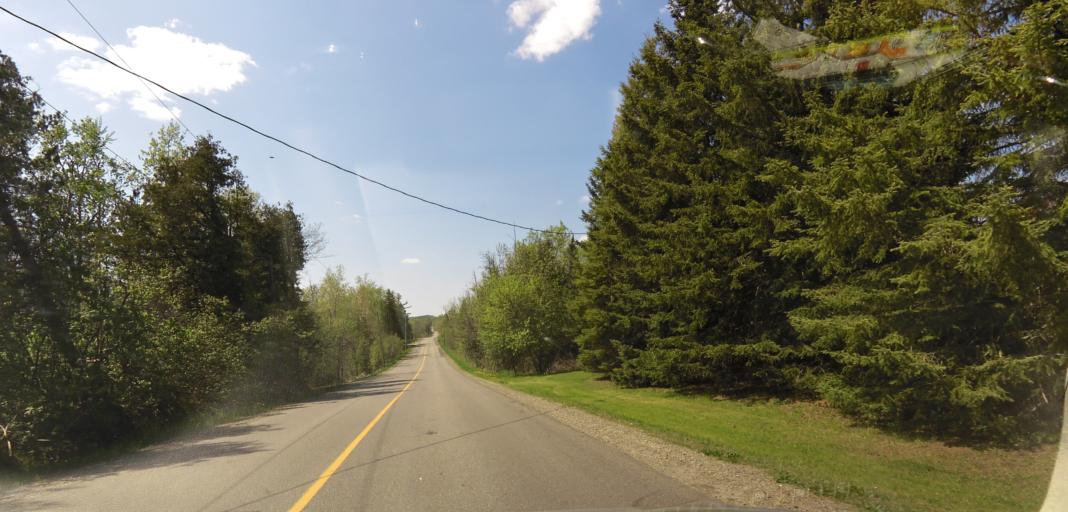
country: CA
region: Ontario
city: Brampton
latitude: 43.8450
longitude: -79.8796
